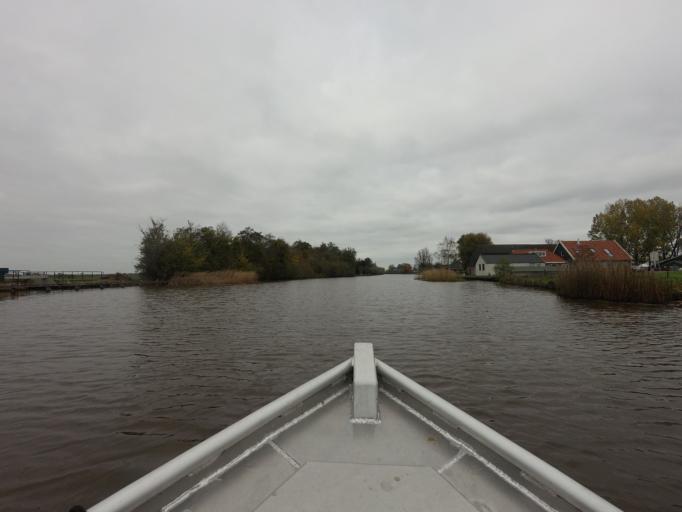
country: NL
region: Overijssel
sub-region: Gemeente Steenwijkerland
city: Blokzijl
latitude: 52.7561
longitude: 5.9954
